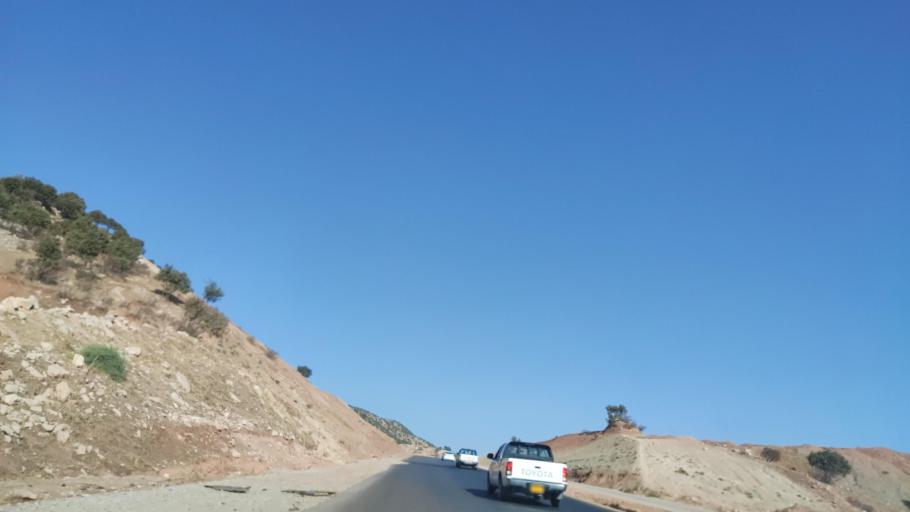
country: IQ
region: Arbil
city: Shaqlawah
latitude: 36.4374
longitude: 44.2912
